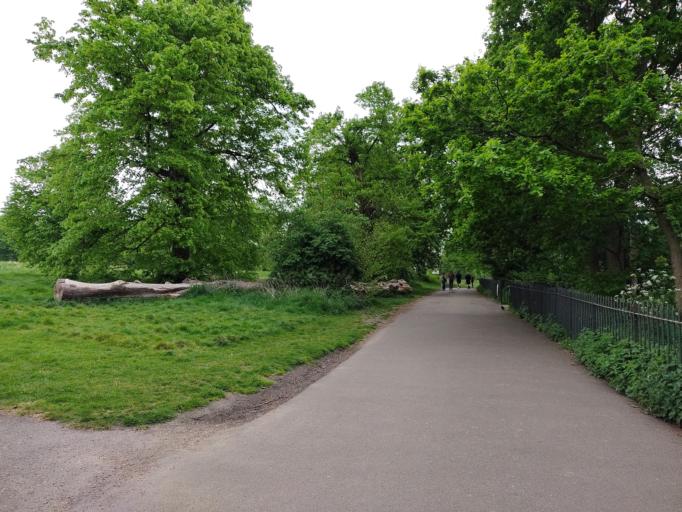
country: GB
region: England
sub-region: Greater London
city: Bayswater
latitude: 51.5086
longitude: -0.1739
